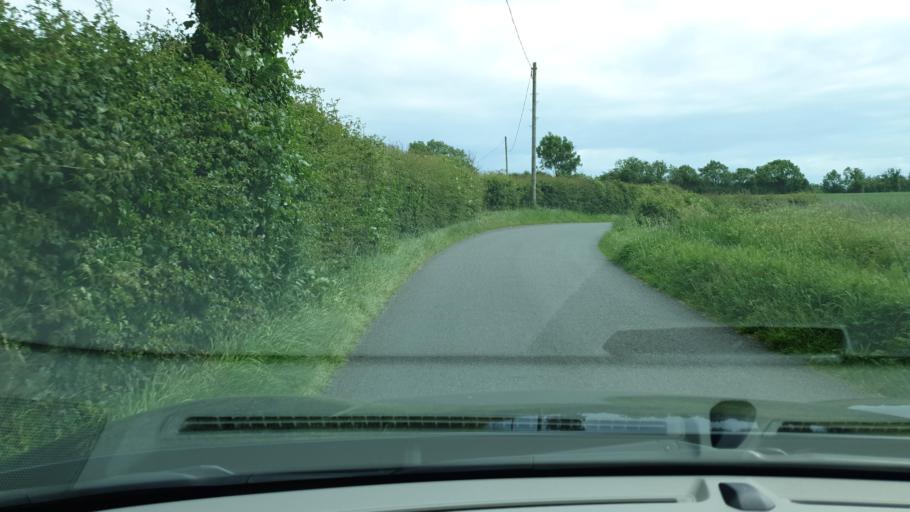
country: IE
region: Leinster
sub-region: An Mhi
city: Ratoath
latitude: 53.4615
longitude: -6.4660
